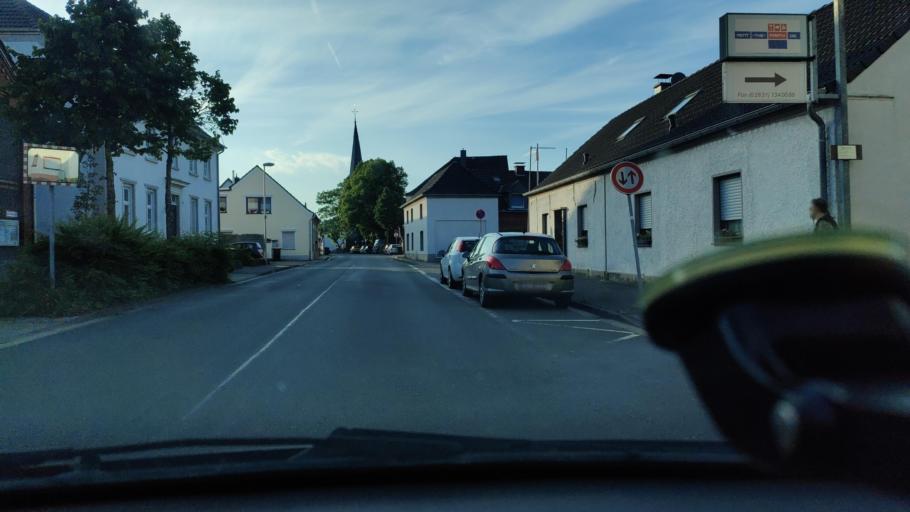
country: DE
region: North Rhine-Westphalia
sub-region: Regierungsbezirk Dusseldorf
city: Rheurdt
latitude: 51.5085
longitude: 6.4719
